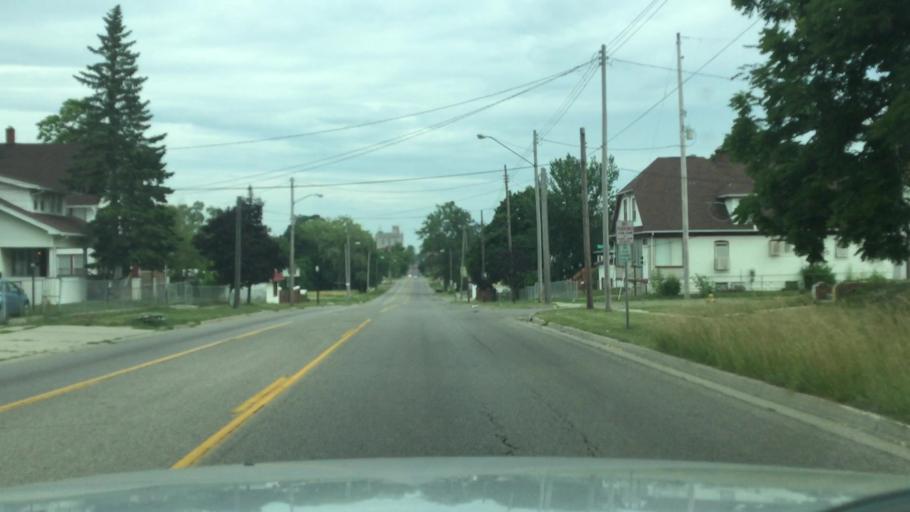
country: US
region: Michigan
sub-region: Genesee County
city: Flint
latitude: 43.0278
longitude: -83.7008
